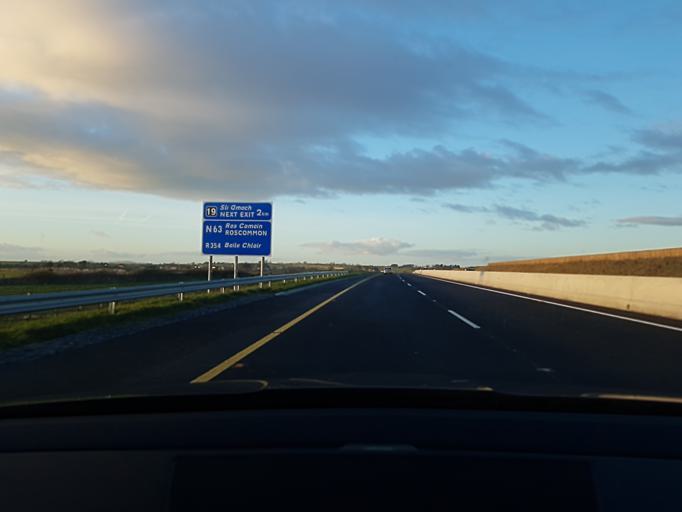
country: IE
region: Connaught
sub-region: County Galway
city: Athenry
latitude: 53.3831
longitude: -8.7995
